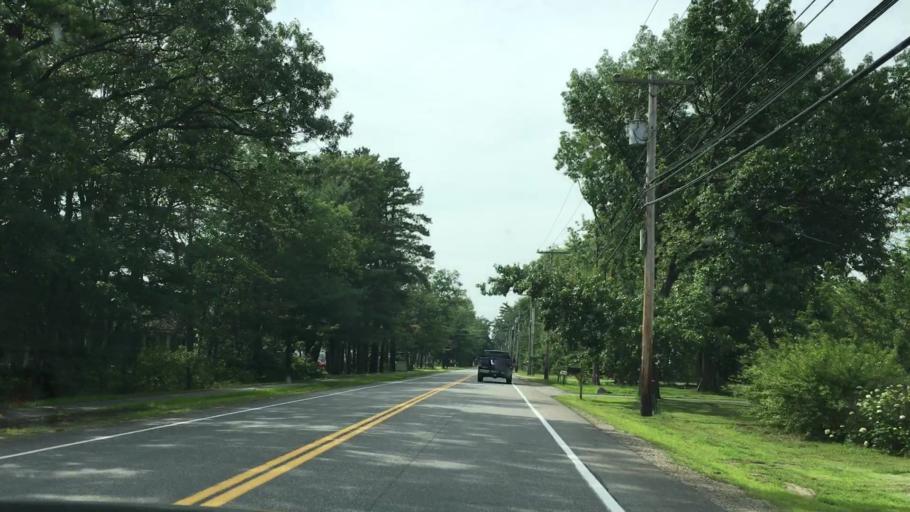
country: US
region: New Hampshire
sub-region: Merrimack County
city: East Concord
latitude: 43.2287
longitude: -71.5126
